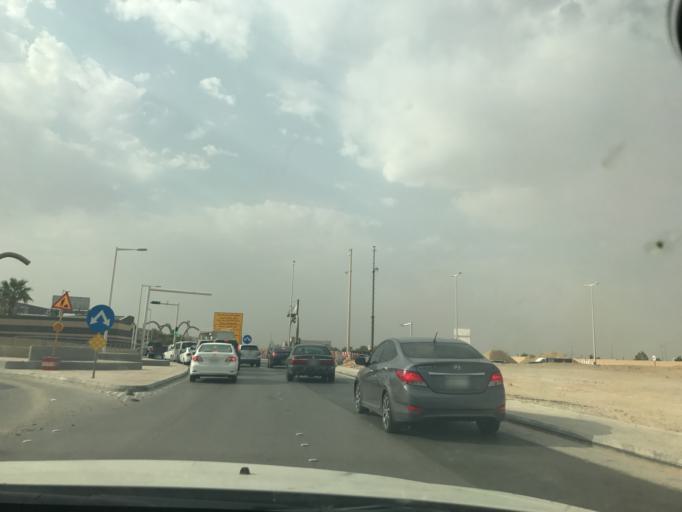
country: SA
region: Ar Riyad
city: Riyadh
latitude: 24.7205
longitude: 46.6936
